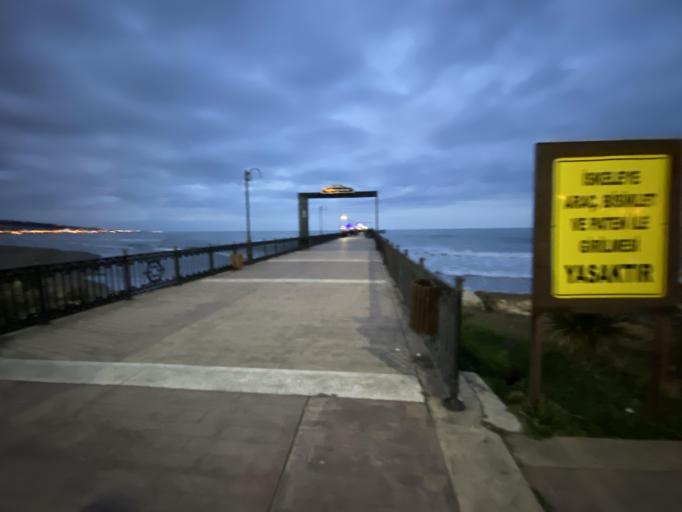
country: TR
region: Samsun
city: Samsun
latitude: 41.3429
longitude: 36.2619
